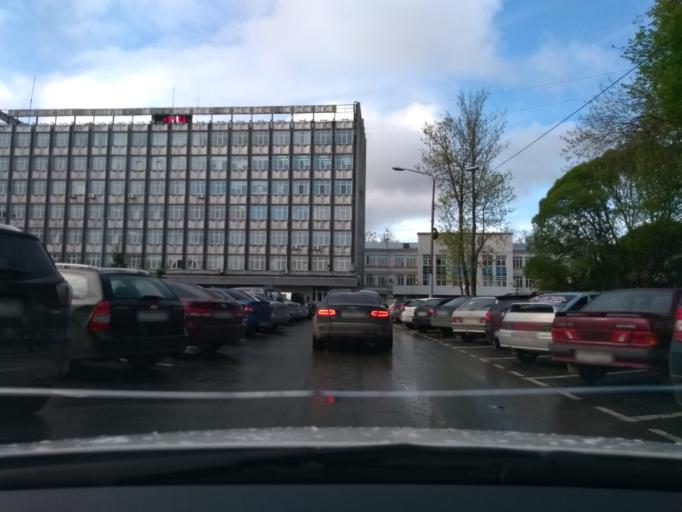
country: RU
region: Perm
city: Perm
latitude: 57.9834
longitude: 56.2528
